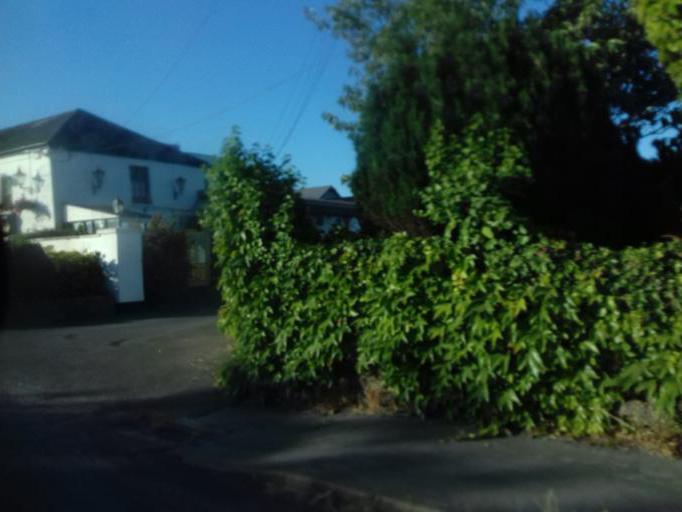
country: IE
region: Leinster
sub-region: Fingal County
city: Blanchardstown
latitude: 53.4400
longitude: -6.3374
